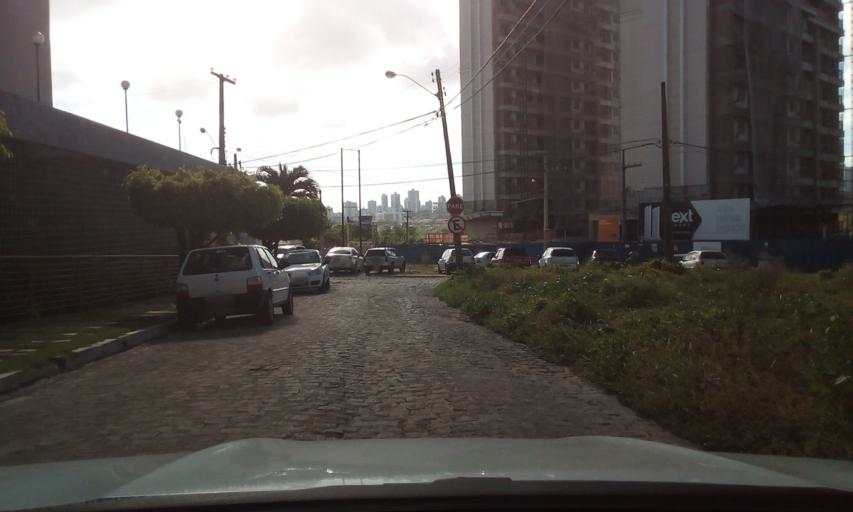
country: BR
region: Paraiba
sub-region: Joao Pessoa
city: Joao Pessoa
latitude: -7.1296
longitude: -34.8296
